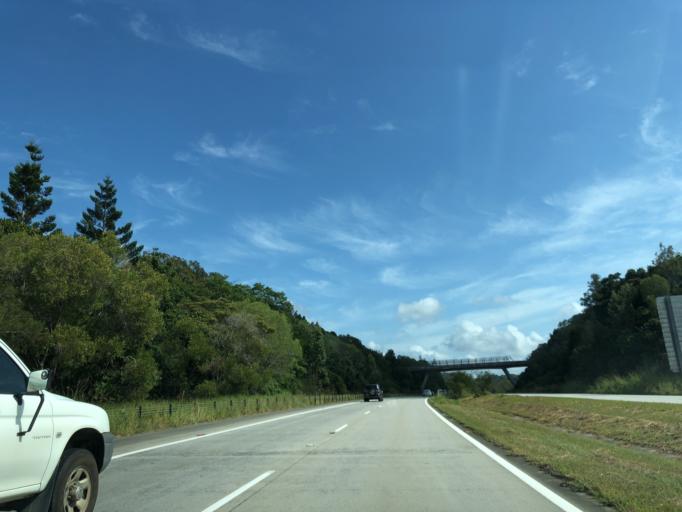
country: AU
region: New South Wales
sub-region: Byron Shire
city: Brunswick Heads
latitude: -28.5746
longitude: 153.5418
